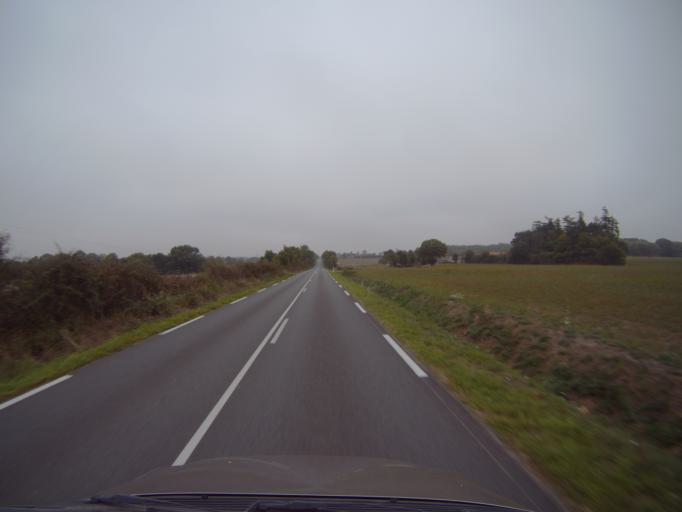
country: FR
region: Pays de la Loire
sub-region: Departement de la Vendee
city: Montaigu
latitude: 46.9891
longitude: -1.2994
